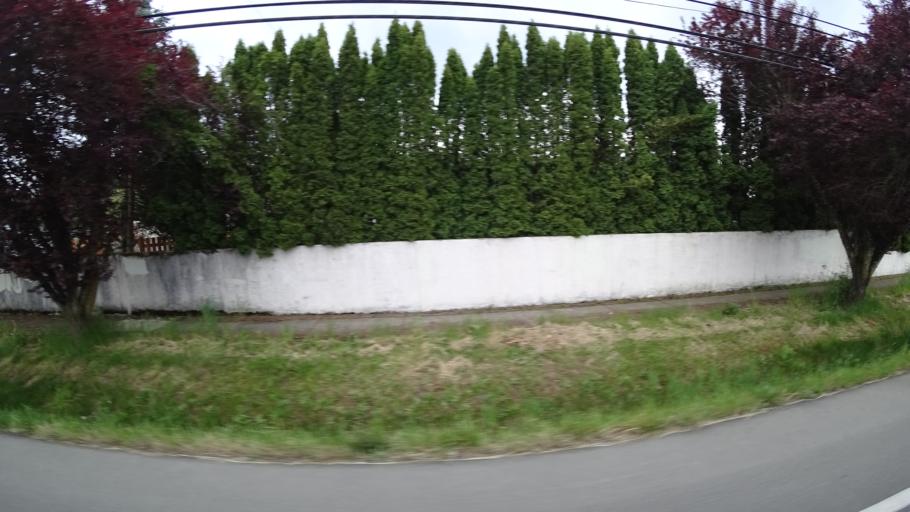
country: US
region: Oregon
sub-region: Washington County
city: Hillsboro
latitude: 45.5316
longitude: -122.9895
